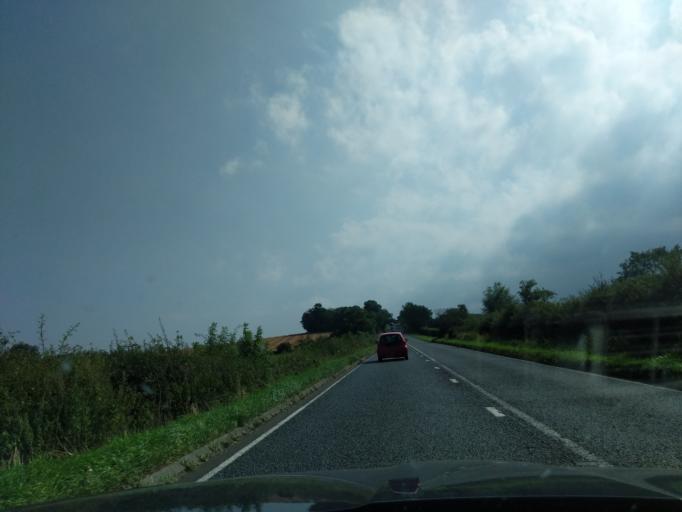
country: GB
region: England
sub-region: Northumberland
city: Longhorsley
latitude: 55.2672
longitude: -1.7774
